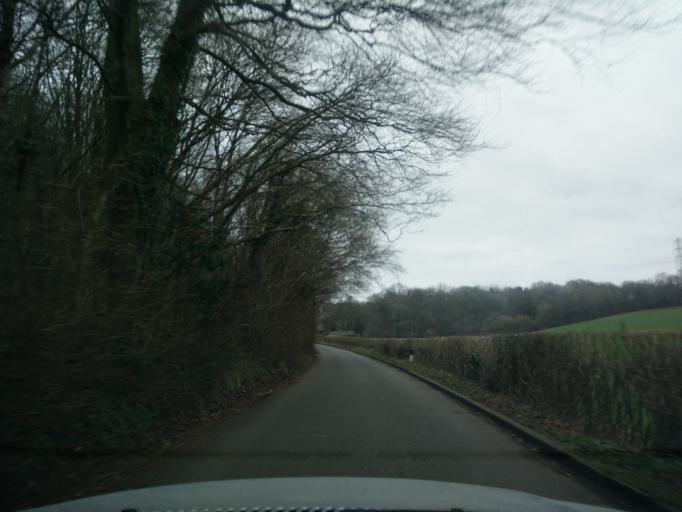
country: GB
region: England
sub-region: Buckinghamshire
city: Great Missenden
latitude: 51.6725
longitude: -0.6768
